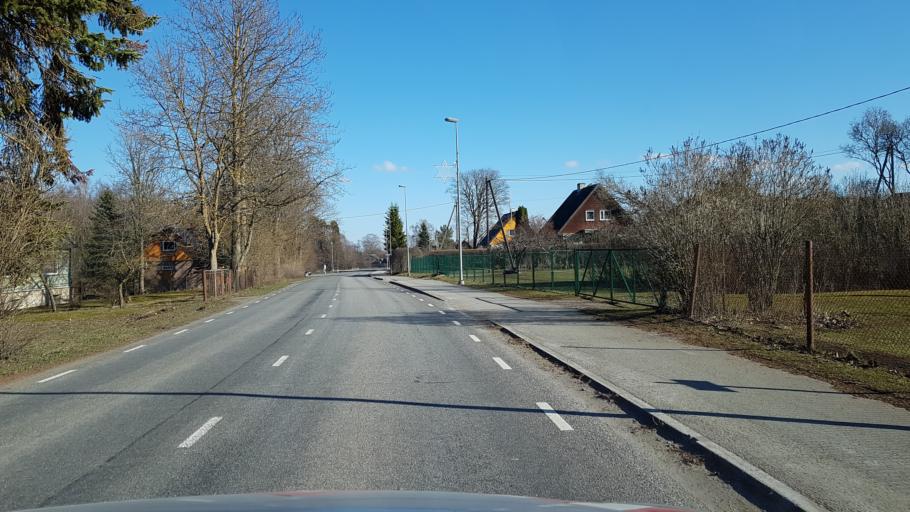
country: EE
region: Laeaene-Virumaa
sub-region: Haljala vald
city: Haljala
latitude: 59.4407
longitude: 26.2587
